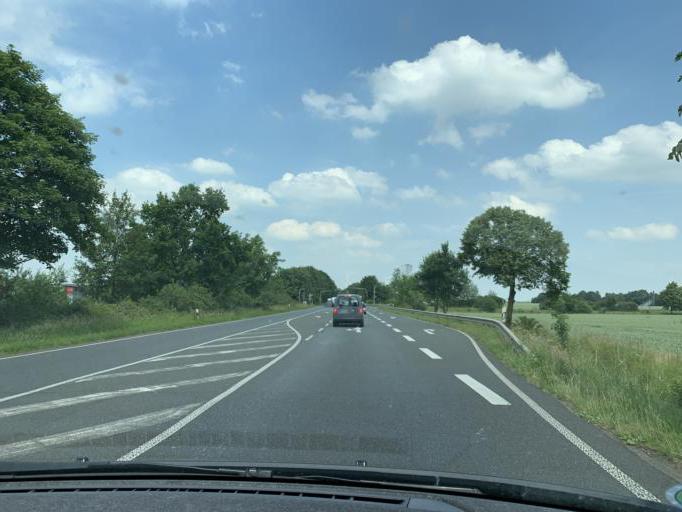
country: DE
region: North Rhine-Westphalia
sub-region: Regierungsbezirk Koln
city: Eschweiler
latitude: 50.8353
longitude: 6.2459
